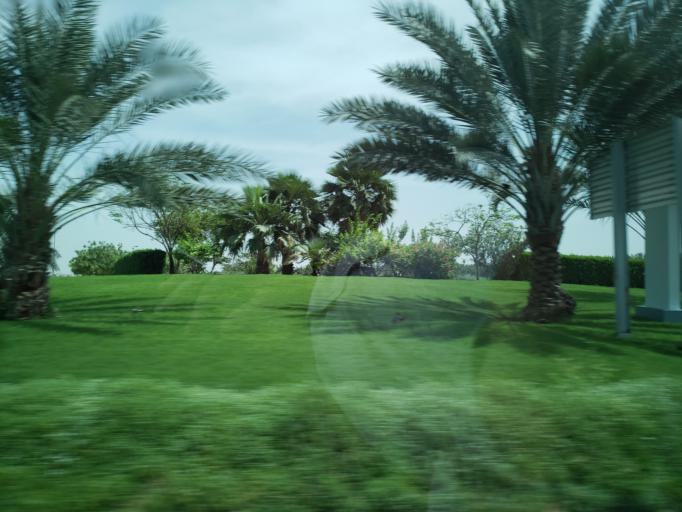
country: AE
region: Ash Shariqah
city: Sharjah
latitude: 25.3228
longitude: 55.5050
